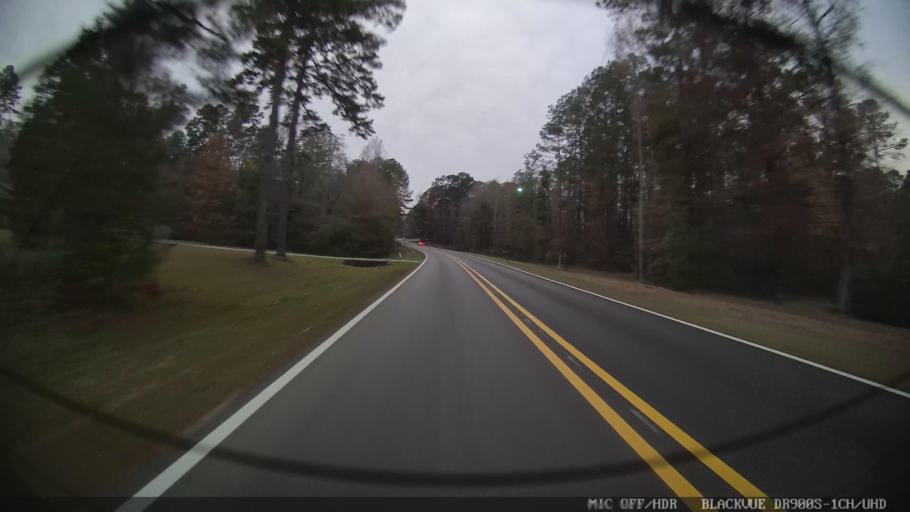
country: US
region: Mississippi
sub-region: Clarke County
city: Quitman
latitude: 32.0434
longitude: -88.7035
